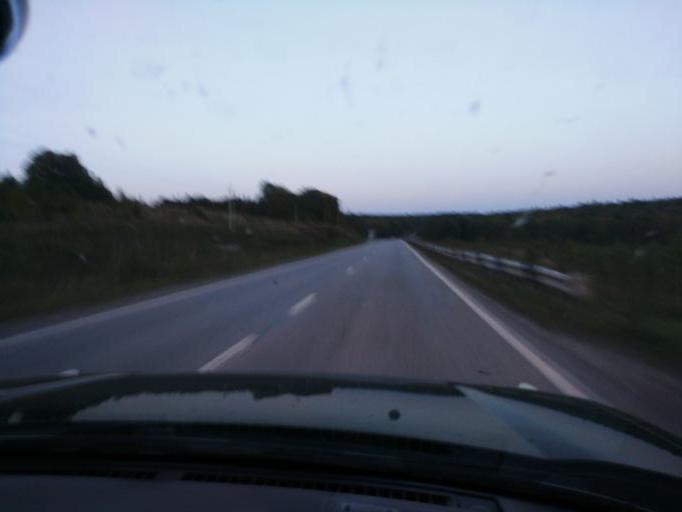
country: RU
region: Perm
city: Verkhnechusovskiye Gorodki
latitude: 58.2814
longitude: 56.9088
